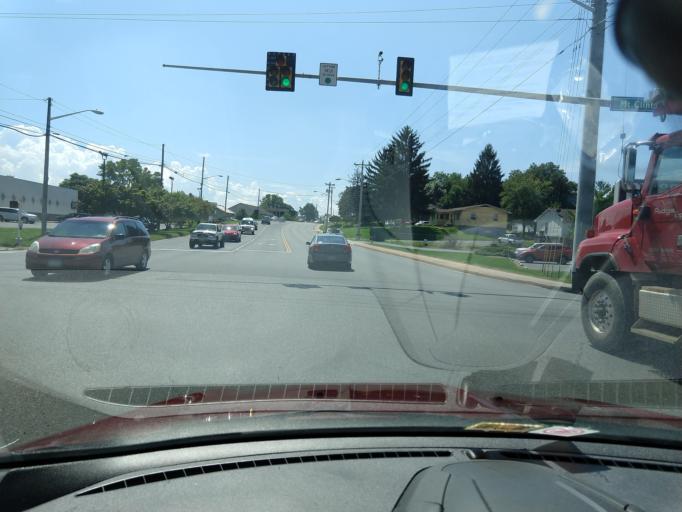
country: US
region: Virginia
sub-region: City of Harrisonburg
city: Harrisonburg
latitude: 38.4687
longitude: -78.8715
